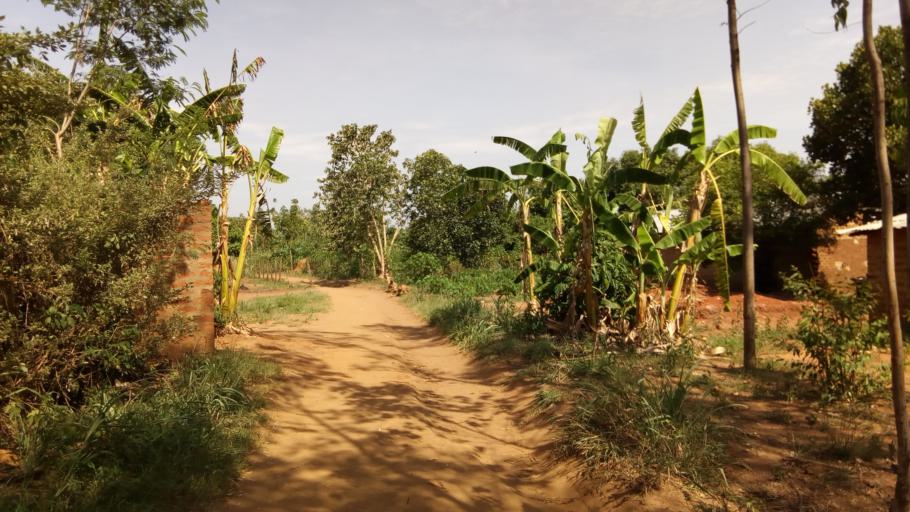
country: UG
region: Northern Region
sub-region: Gulu District
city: Gulu
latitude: 2.7963
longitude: 32.3171
